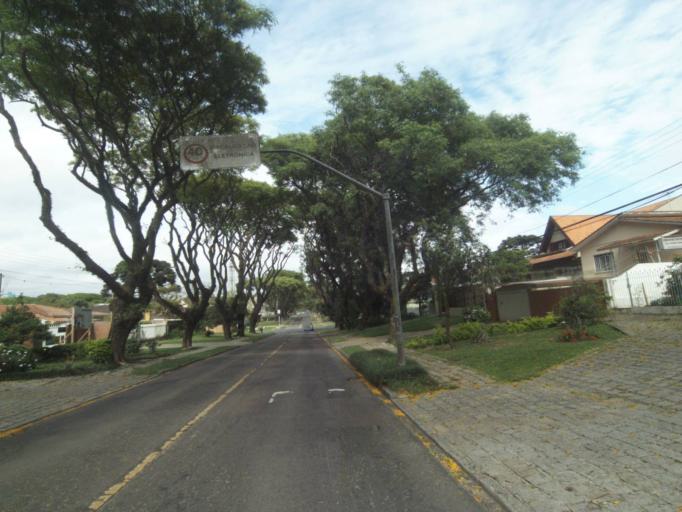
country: BR
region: Parana
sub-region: Curitiba
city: Curitiba
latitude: -25.4254
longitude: -49.2350
